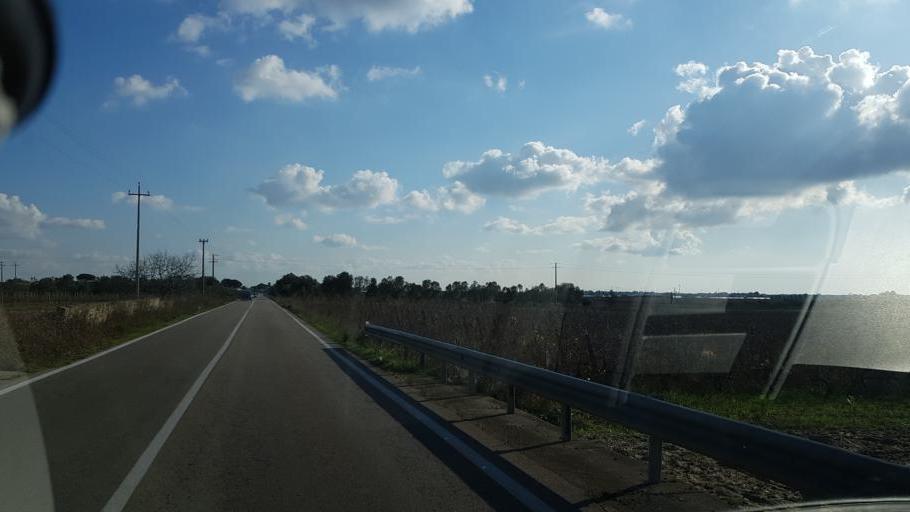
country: IT
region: Apulia
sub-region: Provincia di Lecce
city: Leverano
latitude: 40.3104
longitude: 17.9852
